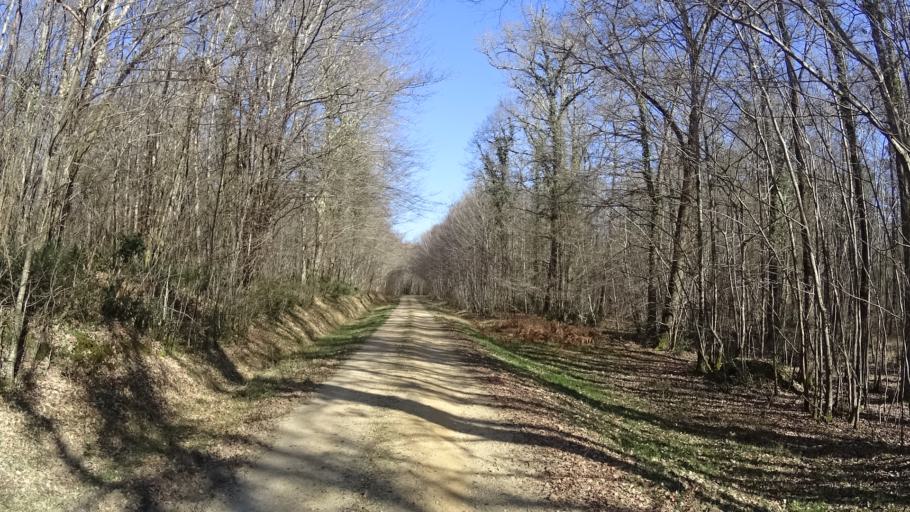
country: FR
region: Aquitaine
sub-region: Departement de la Dordogne
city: Montpon-Menesterol
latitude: 45.0971
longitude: 0.1918
